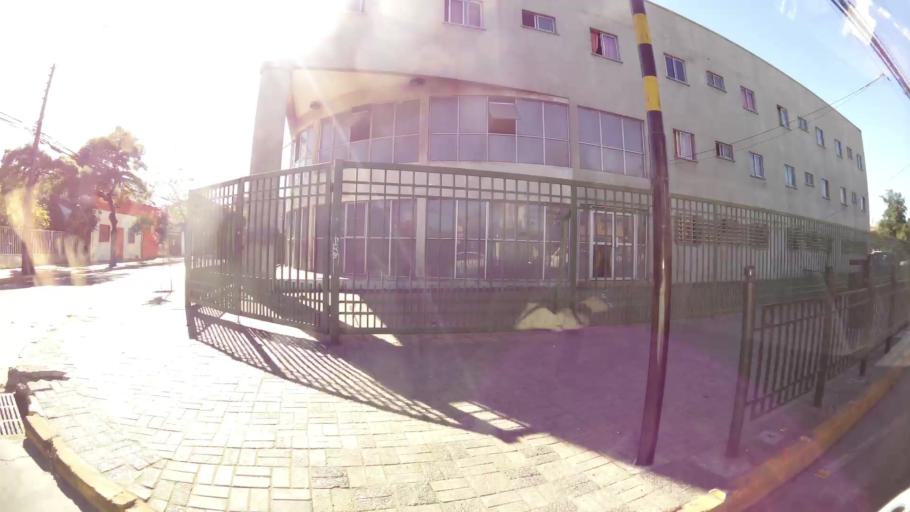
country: CL
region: O'Higgins
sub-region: Provincia de Cachapoal
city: Rancagua
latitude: -34.1661
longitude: -70.7455
